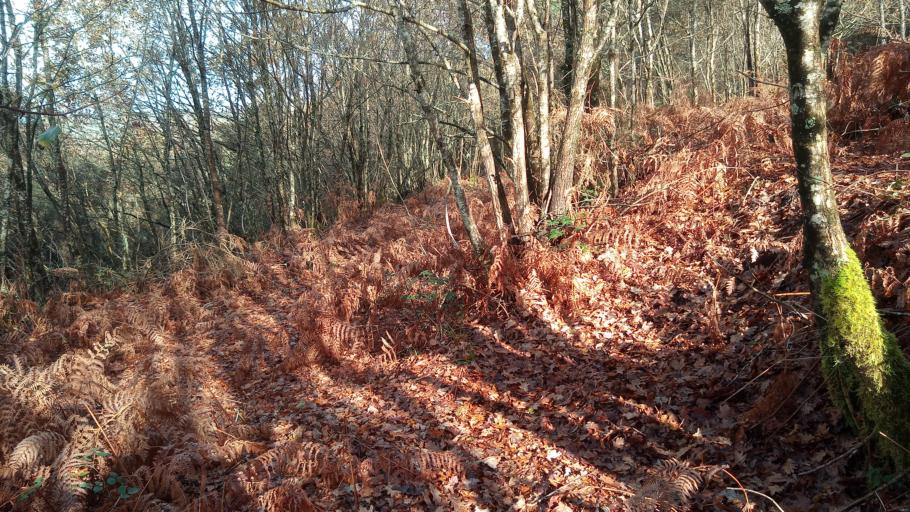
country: PT
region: Viana do Castelo
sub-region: Paredes de Coura
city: Paredes de Coura
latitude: 41.8977
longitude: -8.6157
